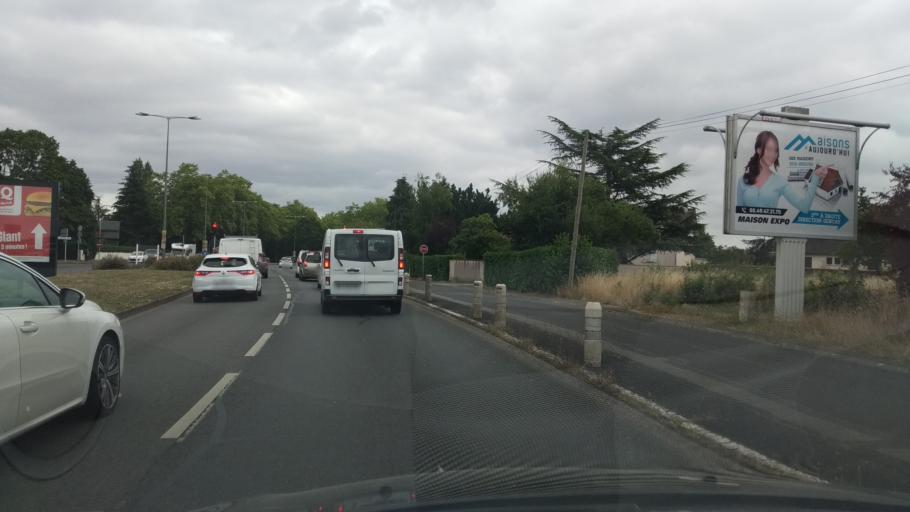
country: FR
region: Poitou-Charentes
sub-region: Departement de la Vienne
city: Saint-Benoit
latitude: 46.5636
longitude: 0.3516
